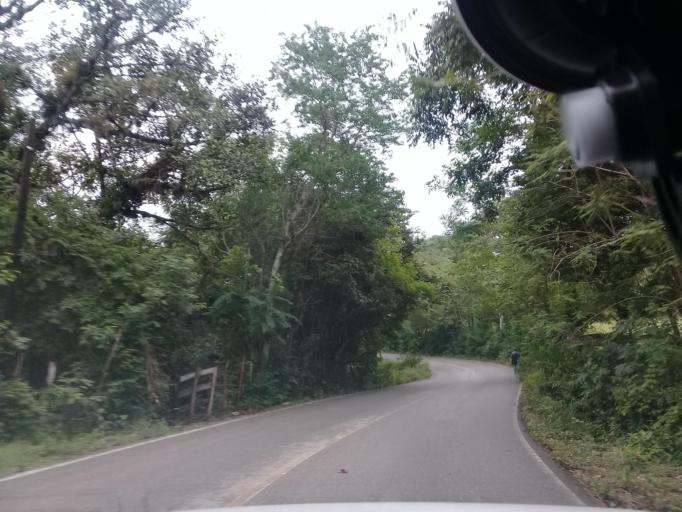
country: MX
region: Veracruz
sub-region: Chalma
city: San Pedro Coyutla
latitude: 21.2084
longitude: -98.4069
